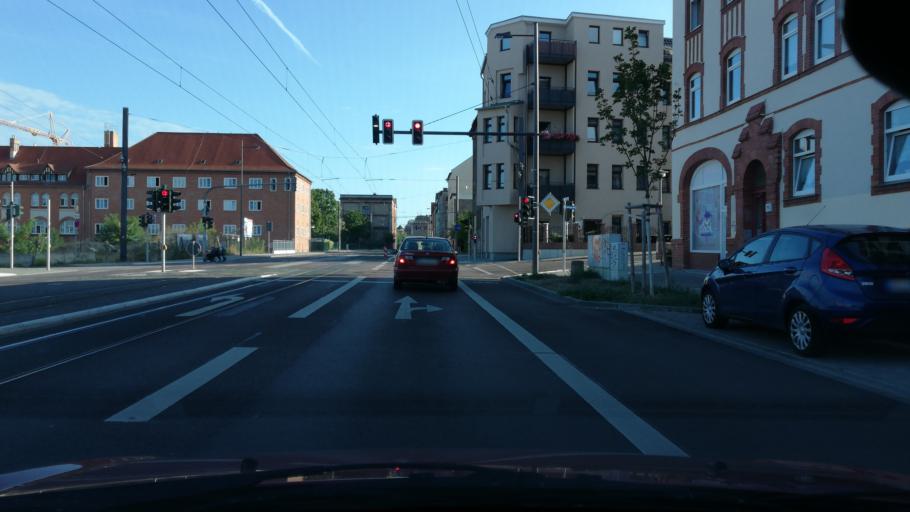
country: DE
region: Saxony-Anhalt
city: Halle Neustadt
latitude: 51.4709
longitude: 11.9591
